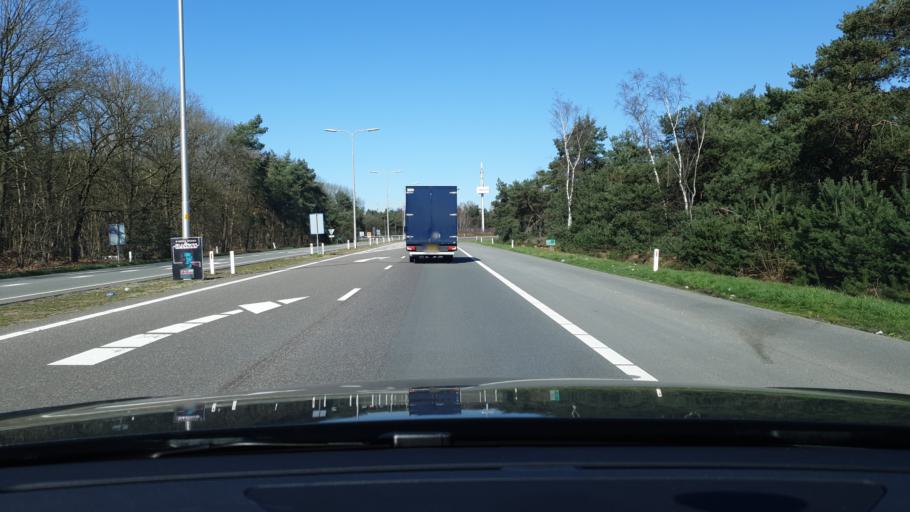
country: NL
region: North Brabant
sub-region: Gemeente Best
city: Best
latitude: 51.4843
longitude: 5.3875
